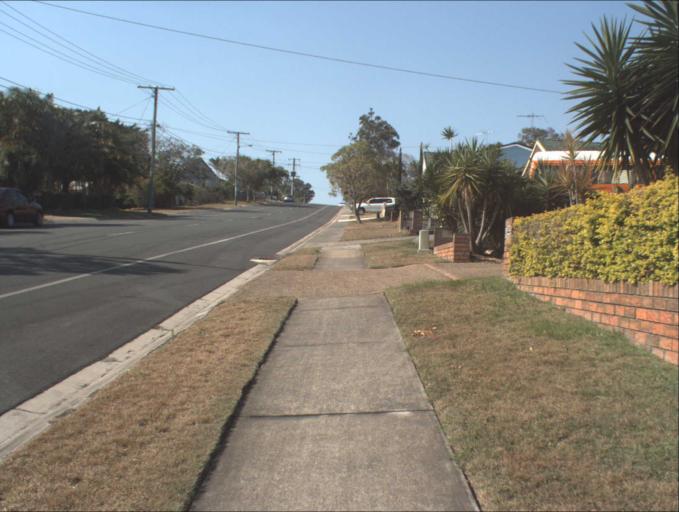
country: AU
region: Queensland
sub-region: Logan
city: Beenleigh
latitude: -27.6966
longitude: 153.1772
